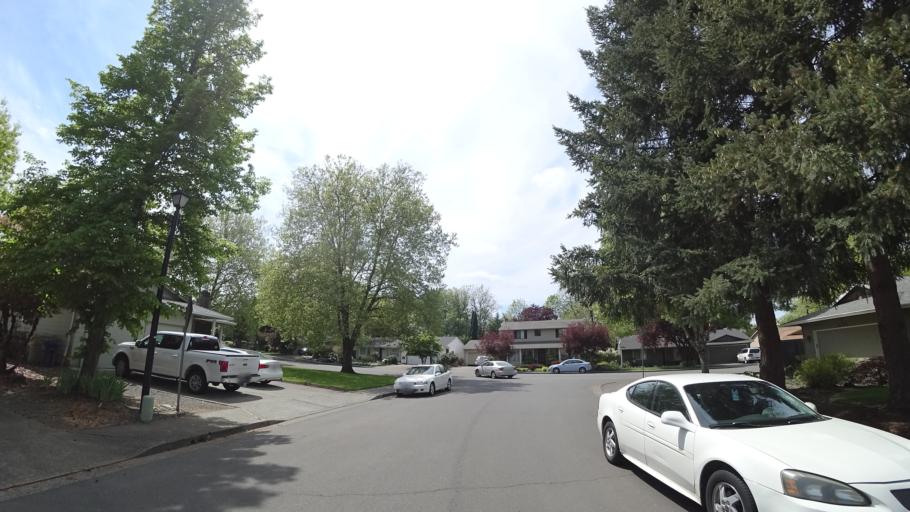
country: US
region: Oregon
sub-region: Washington County
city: Aloha
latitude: 45.4692
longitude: -122.8871
